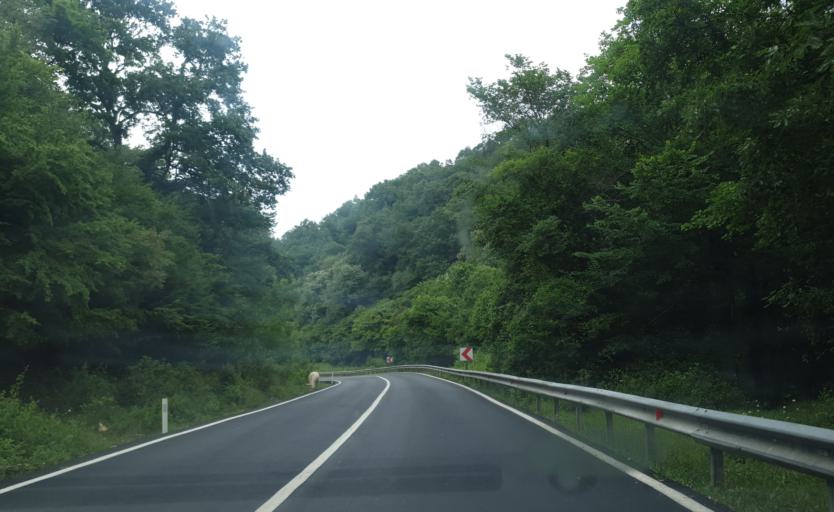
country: TR
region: Kirklareli
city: Salmydessus
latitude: 41.6128
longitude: 28.0901
